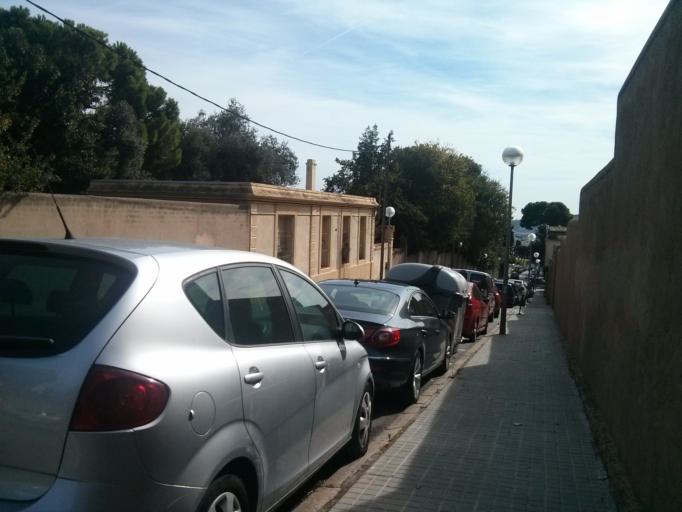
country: ES
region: Catalonia
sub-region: Provincia de Barcelona
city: Sarria-Sant Gervasi
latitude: 41.4081
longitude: 2.1246
